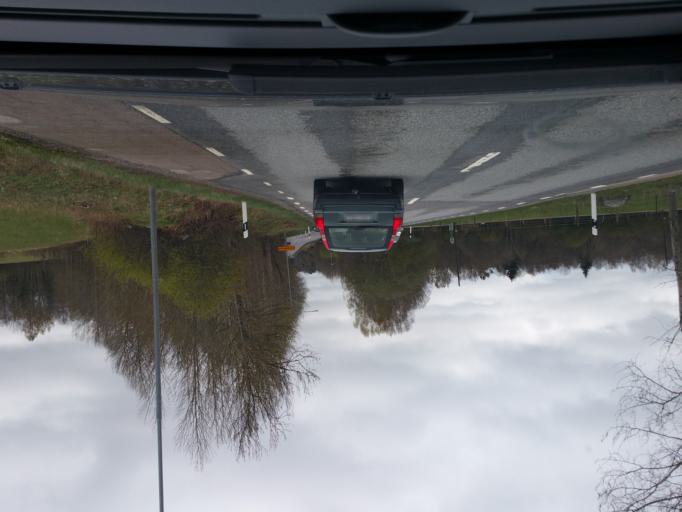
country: SE
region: Kronoberg
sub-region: Vaxjo Kommun
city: Lammhult
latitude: 57.1585
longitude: 14.5922
